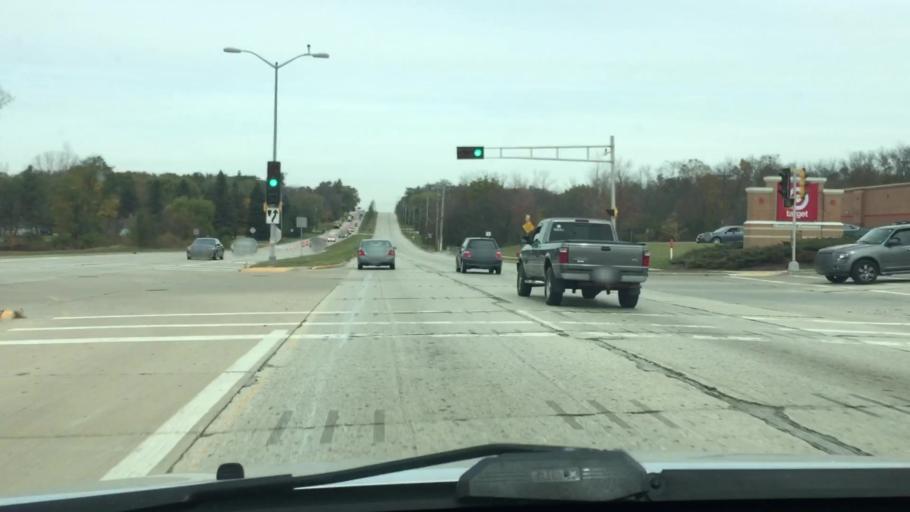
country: US
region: Wisconsin
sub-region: Waukesha County
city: New Berlin
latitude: 42.9579
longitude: -88.1089
